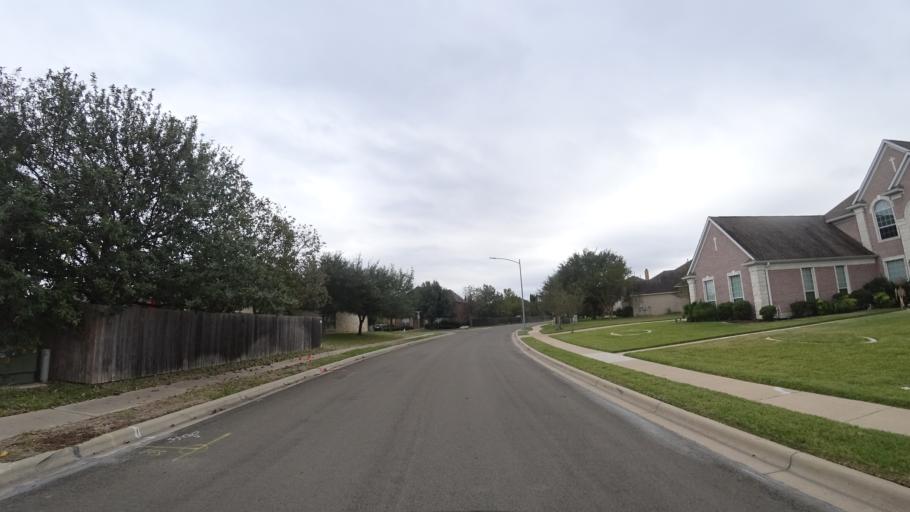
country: US
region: Texas
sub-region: Travis County
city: Shady Hollow
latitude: 30.1522
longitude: -97.8615
